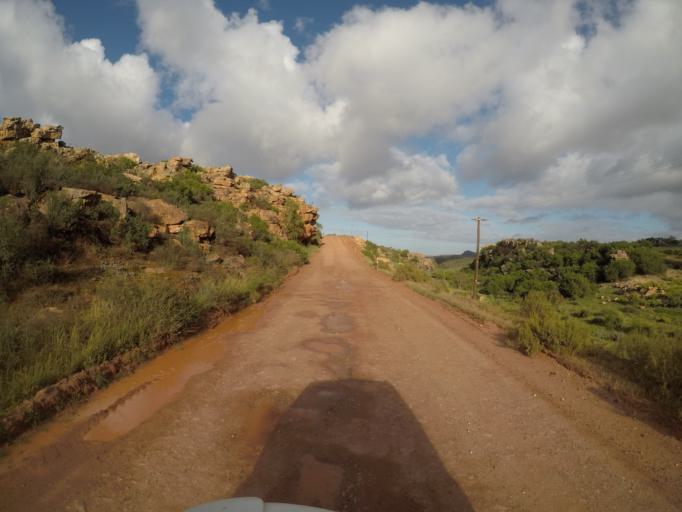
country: ZA
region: Western Cape
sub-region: West Coast District Municipality
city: Clanwilliam
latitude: -32.3404
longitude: 18.7629
